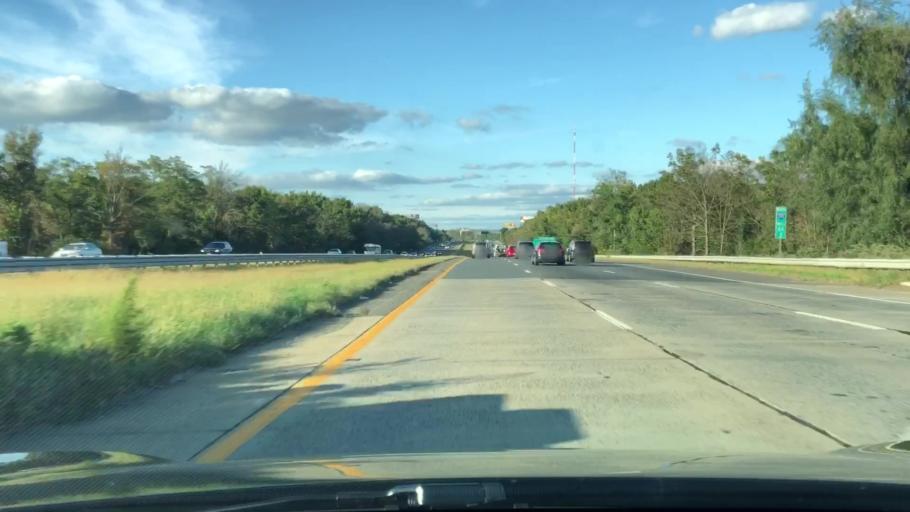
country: US
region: New Jersey
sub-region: Mercer County
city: Mercerville
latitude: 40.2641
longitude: -74.6926
